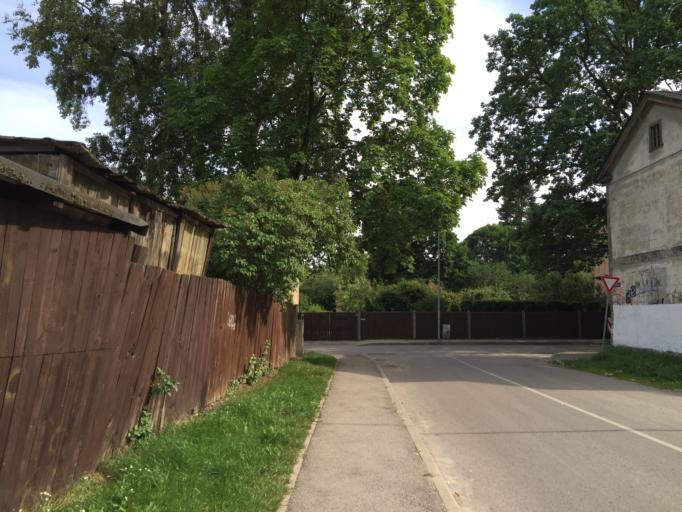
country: LV
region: Marupe
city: Marupe
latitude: 56.9381
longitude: 24.0636
